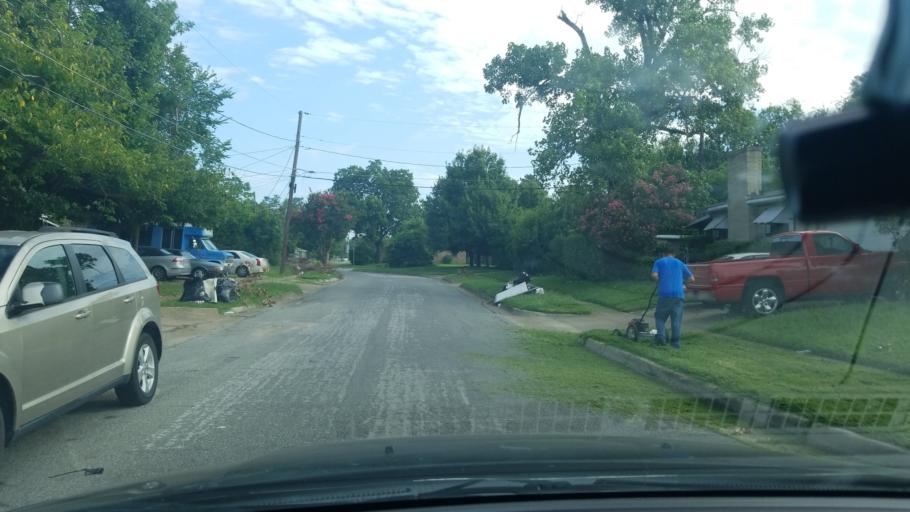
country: US
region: Texas
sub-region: Dallas County
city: Balch Springs
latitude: 32.7523
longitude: -96.6601
